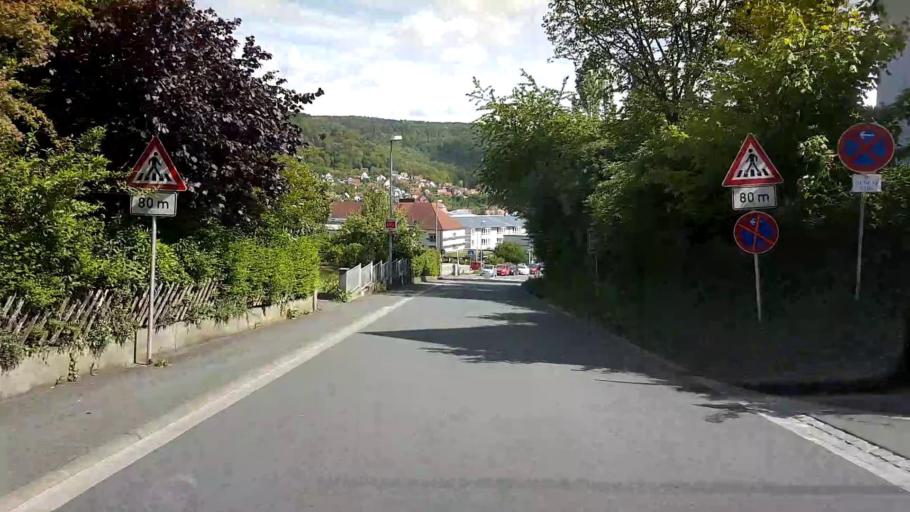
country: DE
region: Bavaria
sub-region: Upper Franconia
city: Ebermannstadt
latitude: 49.7807
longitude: 11.1777
